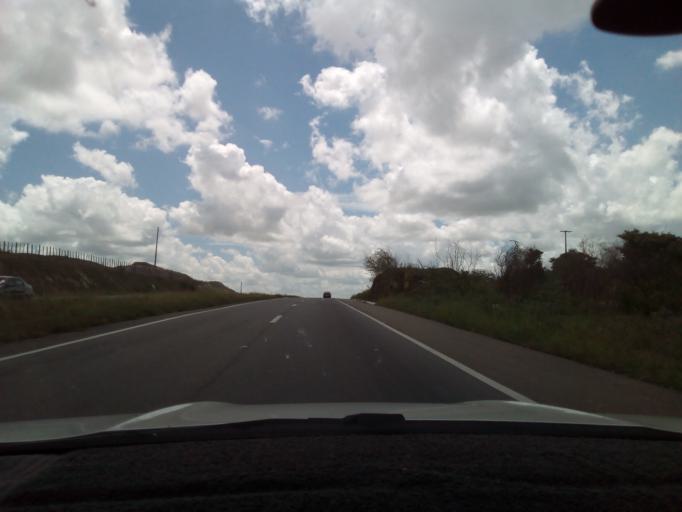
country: BR
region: Paraiba
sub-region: Gurinhem
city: Gurinhem
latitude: -7.1774
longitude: -35.4164
